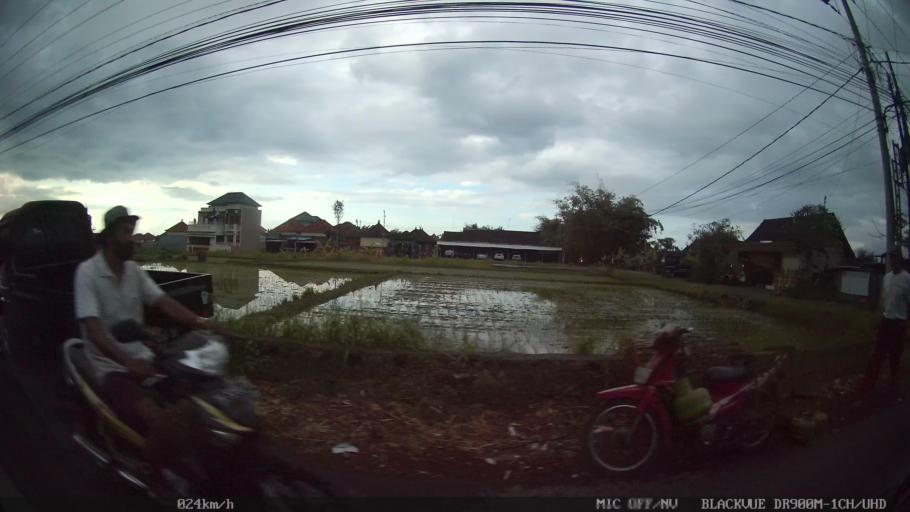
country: ID
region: Bali
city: Banjar Pasekan
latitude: -8.6160
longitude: 115.2765
